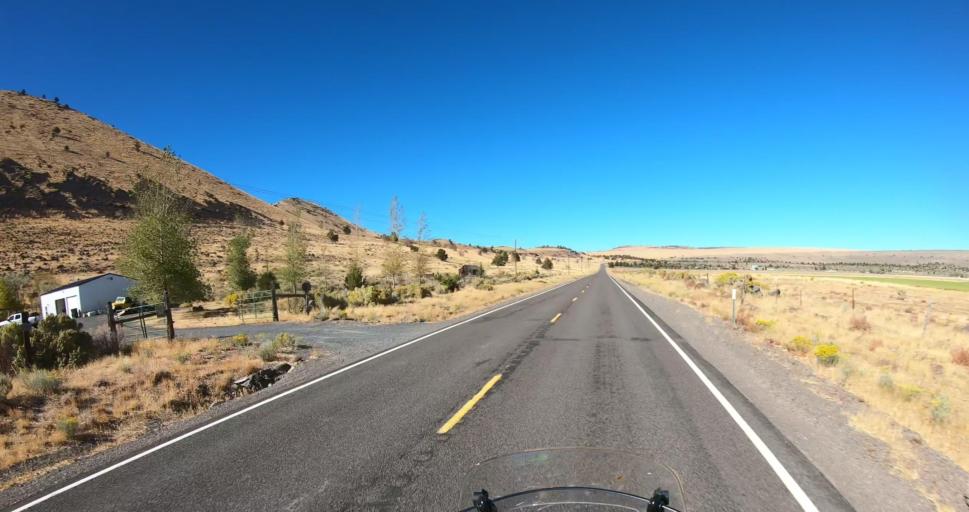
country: US
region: Oregon
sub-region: Lake County
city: Lakeview
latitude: 42.9939
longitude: -120.7762
